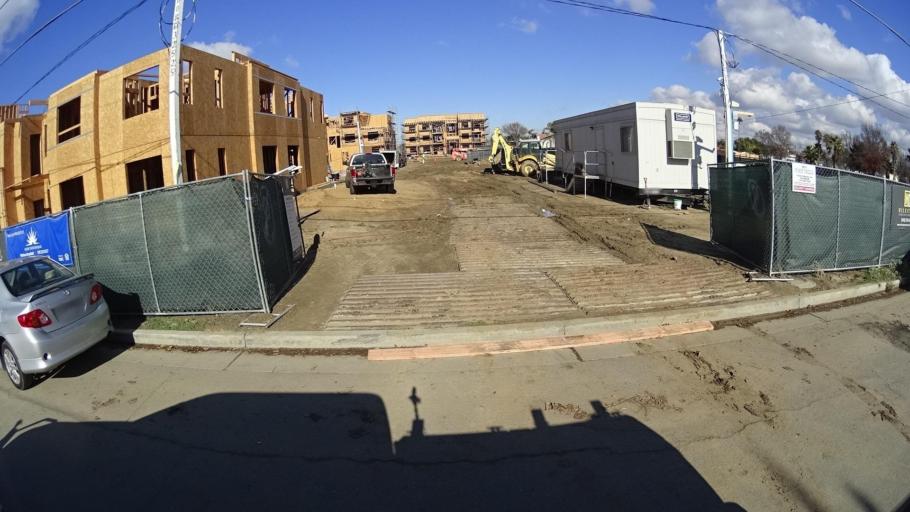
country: US
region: California
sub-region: Kern County
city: McFarland
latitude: 35.6742
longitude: -119.2375
